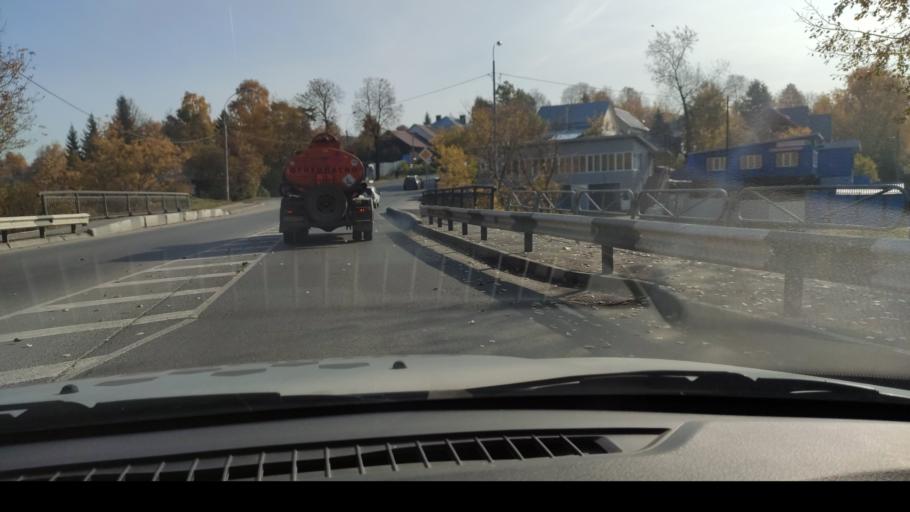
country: RU
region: Perm
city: Perm
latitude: 58.0403
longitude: 56.3260
